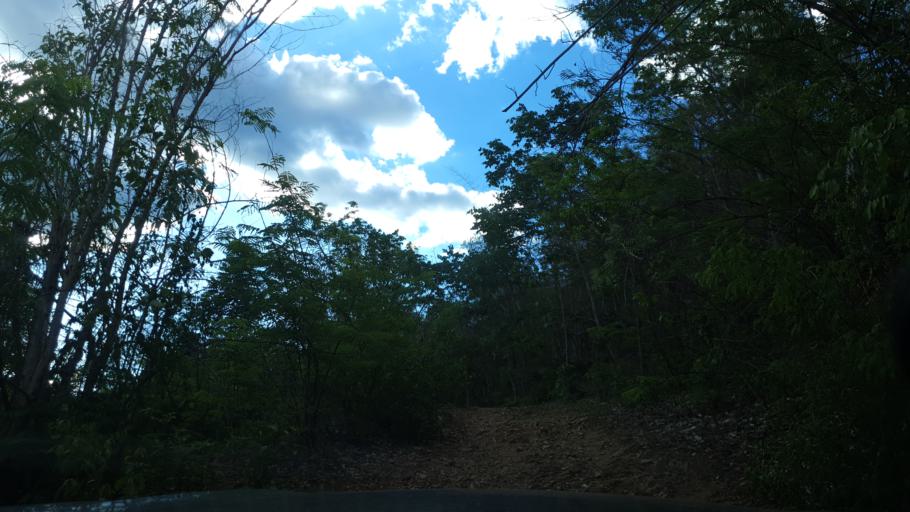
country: TH
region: Lampang
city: Sop Prap
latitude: 17.8888
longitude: 99.2857
